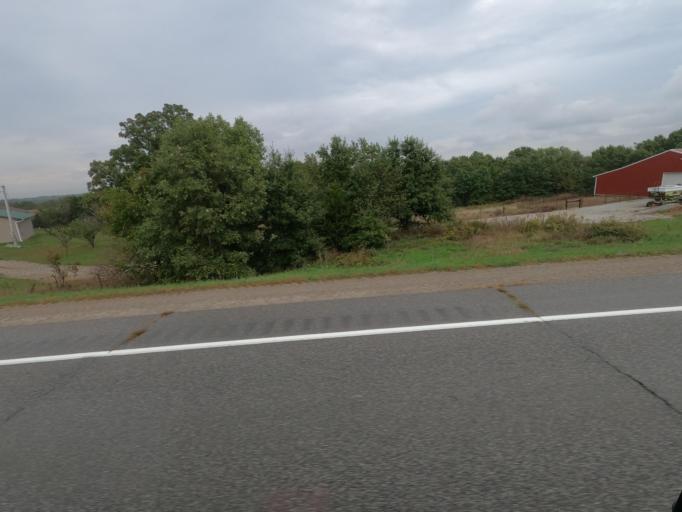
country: US
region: Iowa
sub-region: Van Buren County
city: Keosauqua
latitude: 40.8164
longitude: -91.9409
